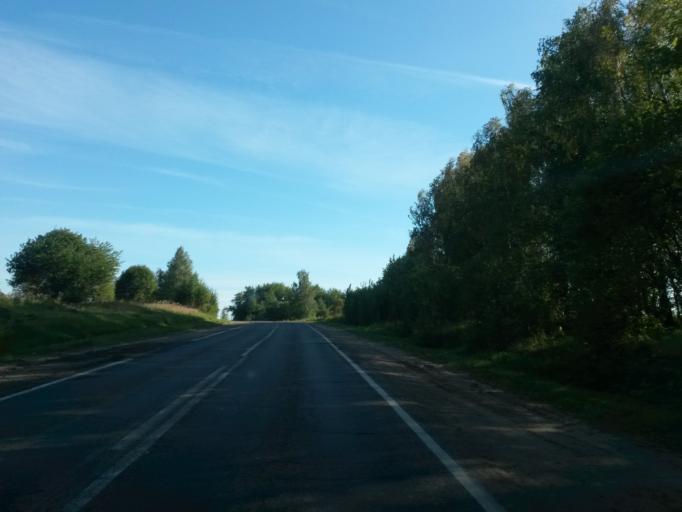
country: RU
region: Jaroslavl
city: Yaroslavl
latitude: 57.5454
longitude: 39.8617
